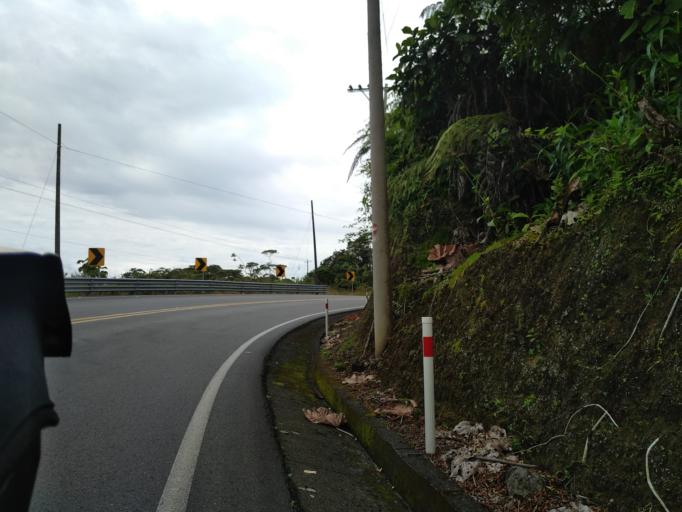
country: EC
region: Pastaza
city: Puyo
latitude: -1.3539
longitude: -77.9254
